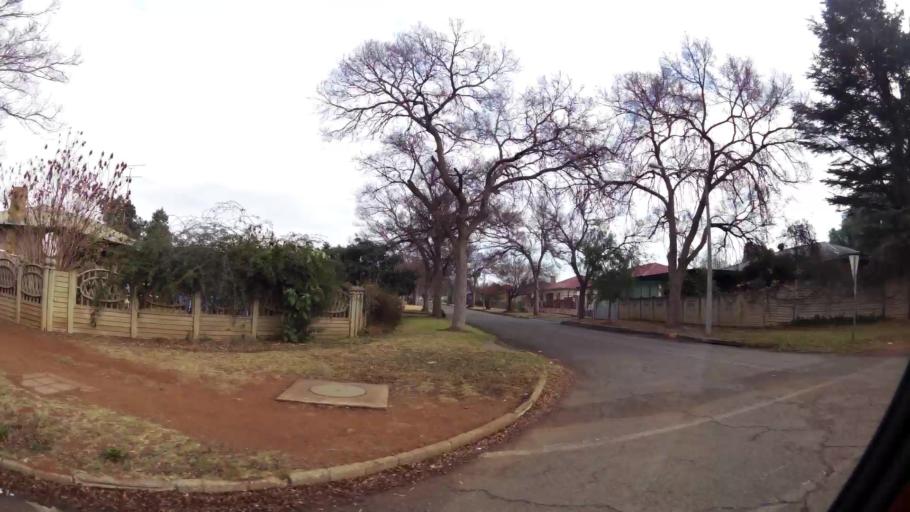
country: ZA
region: Gauteng
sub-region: Sedibeng District Municipality
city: Vanderbijlpark
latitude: -26.6934
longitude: 27.8190
